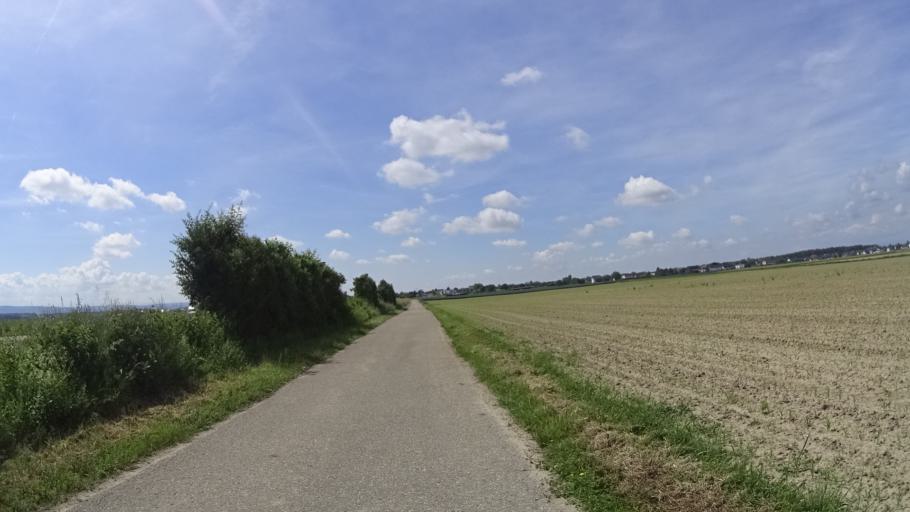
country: DE
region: Baden-Wuerttemberg
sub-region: Freiburg Region
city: Meissenheim
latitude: 48.4451
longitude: 7.8132
